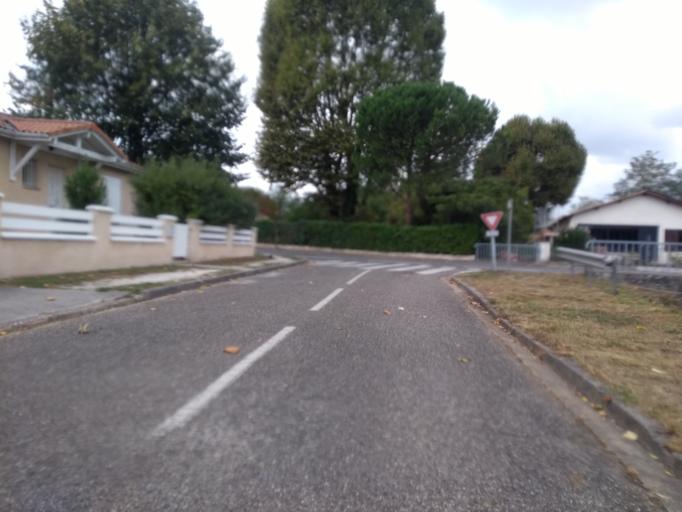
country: FR
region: Aquitaine
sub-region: Departement de la Gironde
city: Merignac
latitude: 44.8259
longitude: -0.6508
